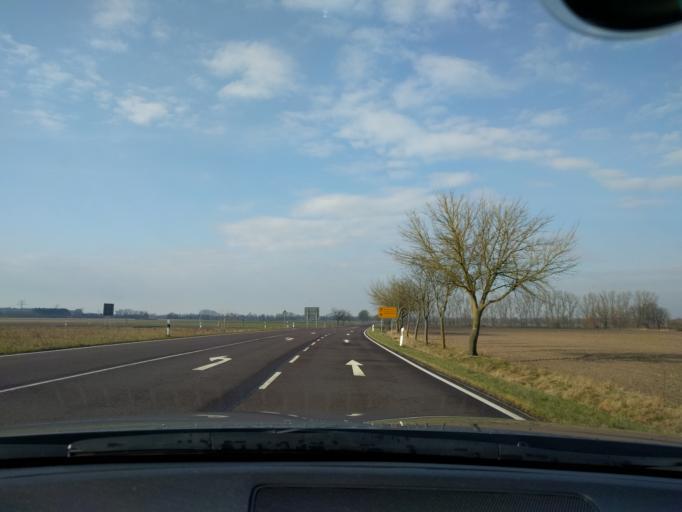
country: DE
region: Saxony-Anhalt
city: Arneburg
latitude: 52.6749
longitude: 11.9674
